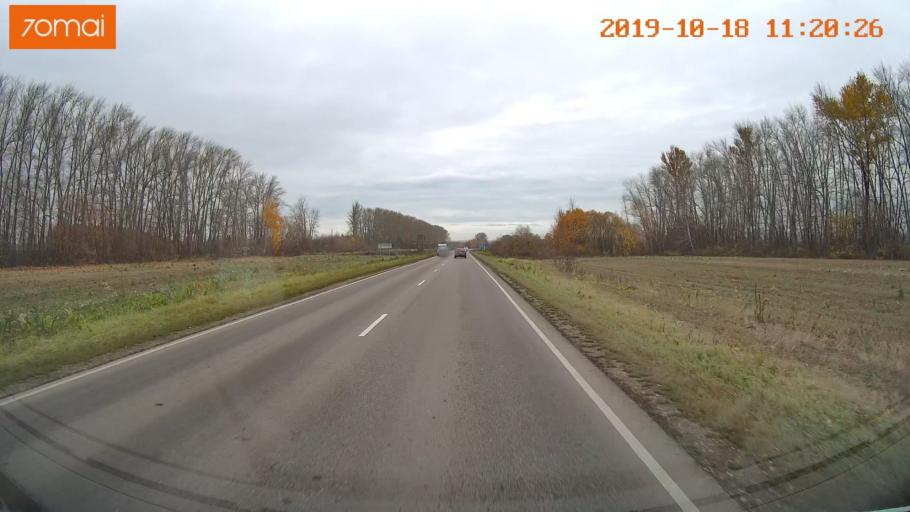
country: RU
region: Tula
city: Kimovsk
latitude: 54.0608
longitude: 38.5586
